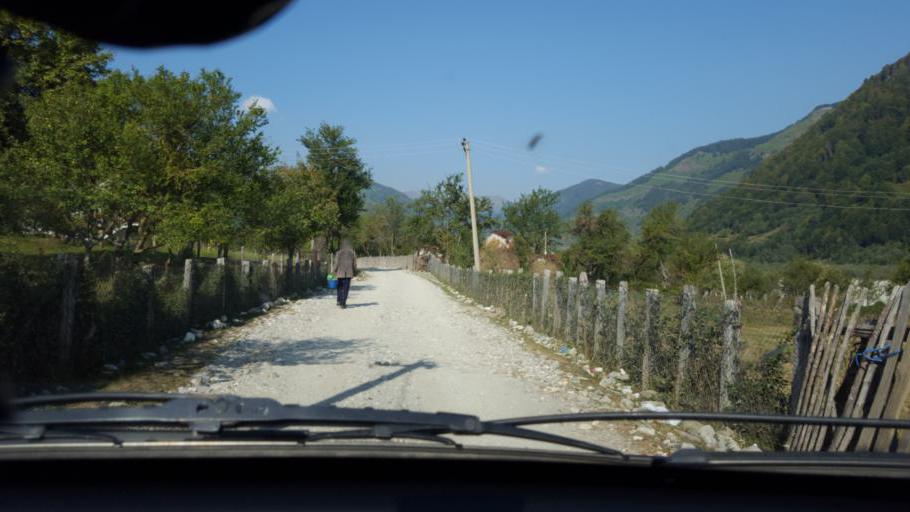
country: ME
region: Andrijevica
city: Andrijevica
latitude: 42.5904
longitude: 19.6910
